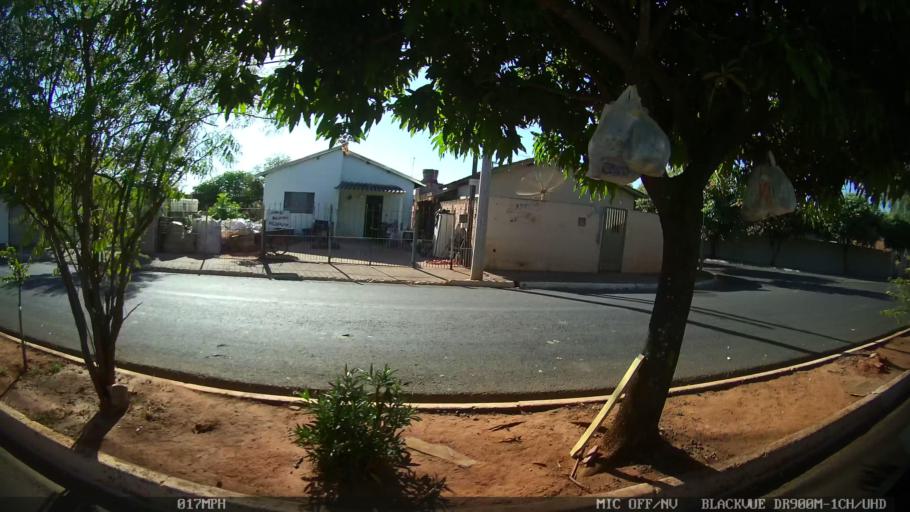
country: BR
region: Sao Paulo
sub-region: Olimpia
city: Olimpia
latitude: -20.7261
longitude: -48.8978
